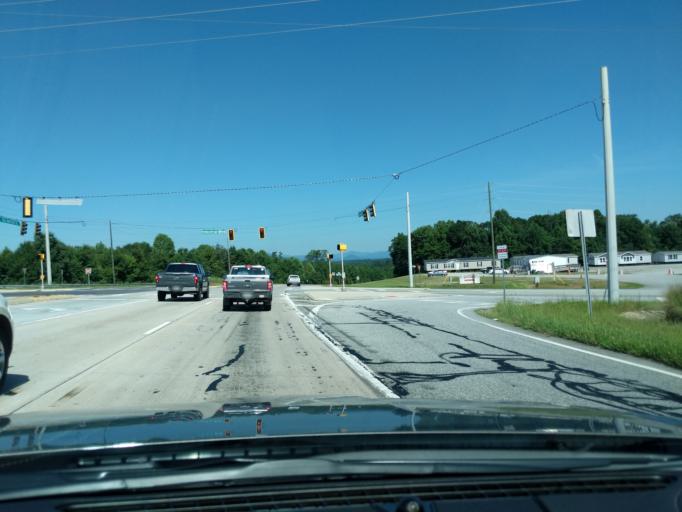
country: US
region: Georgia
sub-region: Habersham County
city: Baldwin
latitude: 34.5003
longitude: -83.5432
